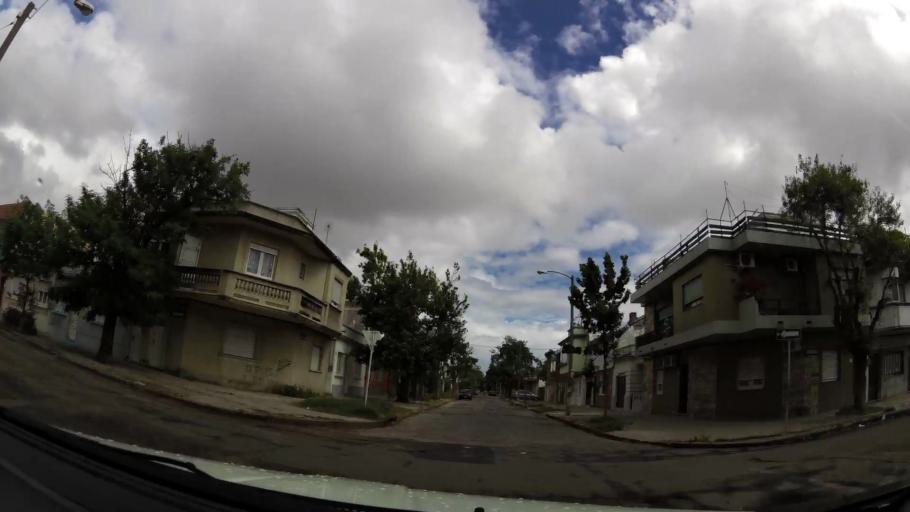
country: UY
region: Montevideo
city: Montevideo
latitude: -34.8730
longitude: -56.1698
